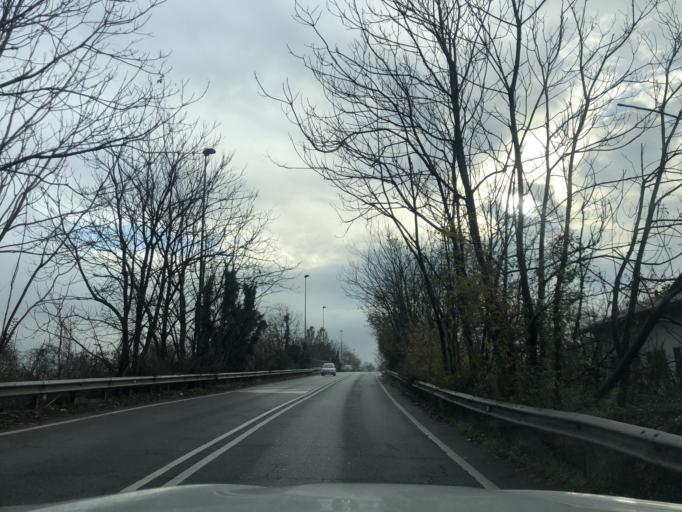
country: IT
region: Lombardy
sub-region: Citta metropolitana di Milano
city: Cologno Monzese
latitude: 45.5532
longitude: 9.2651
